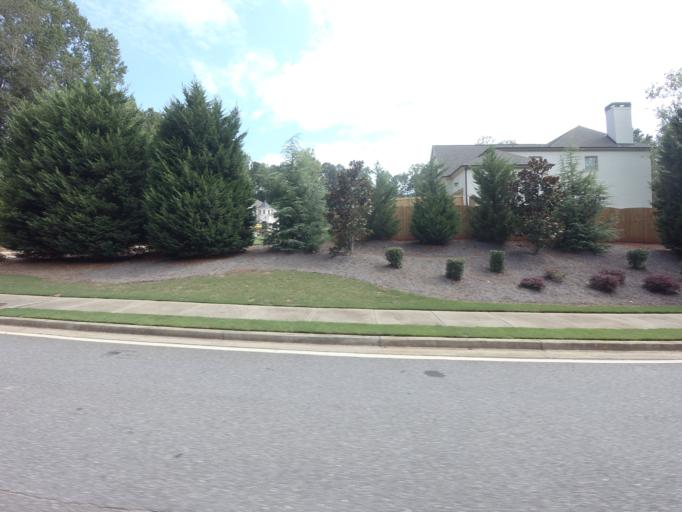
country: US
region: Georgia
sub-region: Fulton County
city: Johns Creek
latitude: 34.0197
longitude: -84.2195
